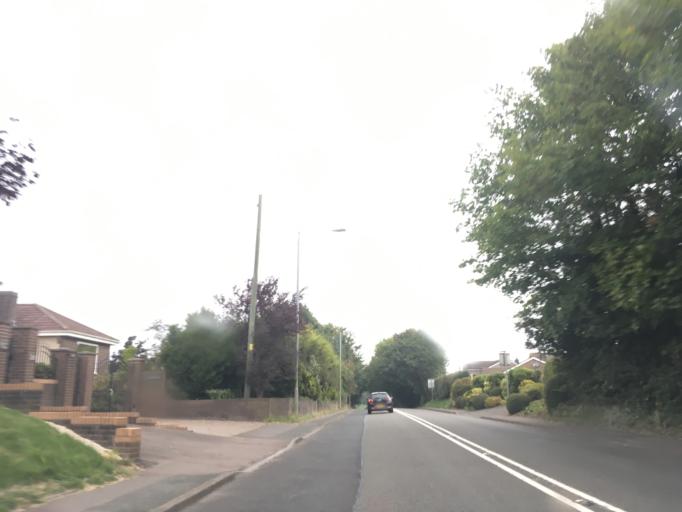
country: GB
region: Wales
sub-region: Monmouthshire
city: Chepstow
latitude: 51.6442
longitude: -2.6896
